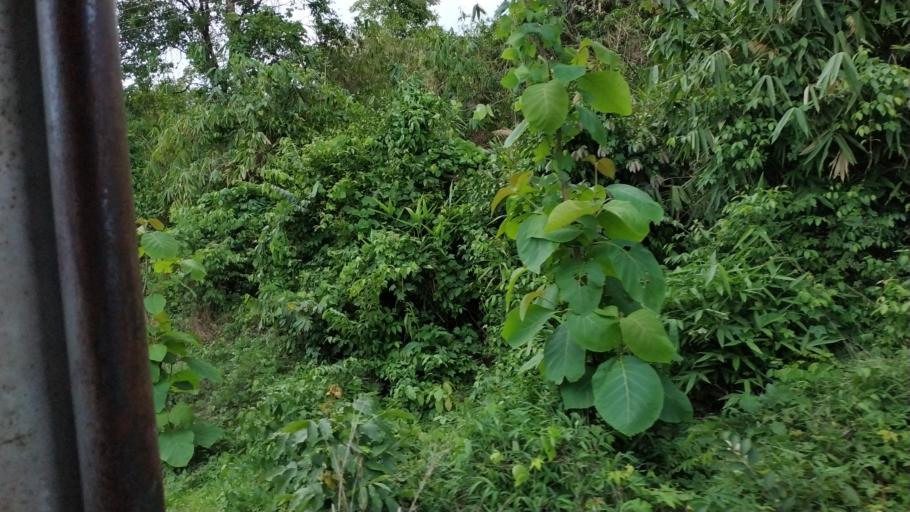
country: MM
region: Mon
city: Kyaikto
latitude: 17.4147
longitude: 97.0719
